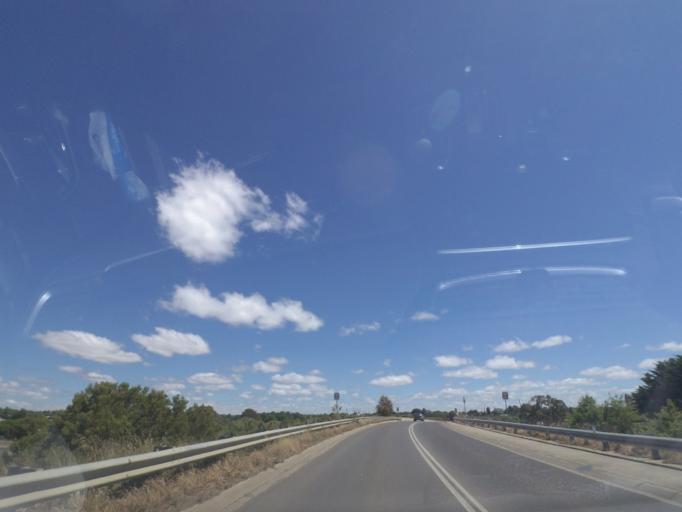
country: AU
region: Victoria
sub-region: Mount Alexander
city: Castlemaine
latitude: -37.2384
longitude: 144.4575
